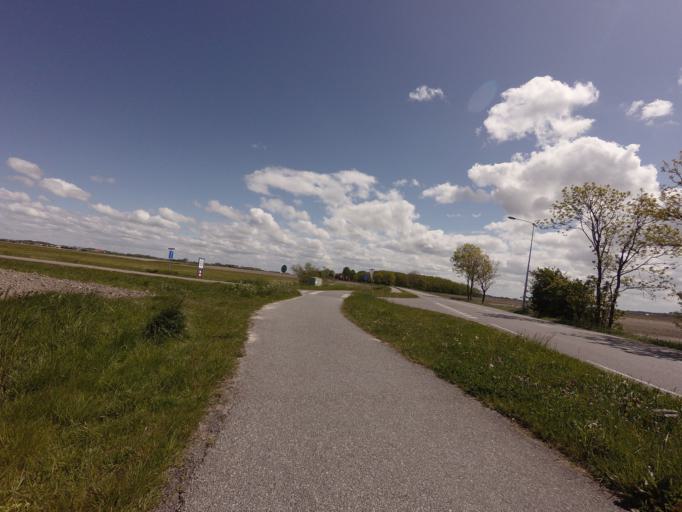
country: NL
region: Friesland
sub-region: Gemeente Harlingen
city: Harlingen
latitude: 53.1386
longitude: 5.4483
